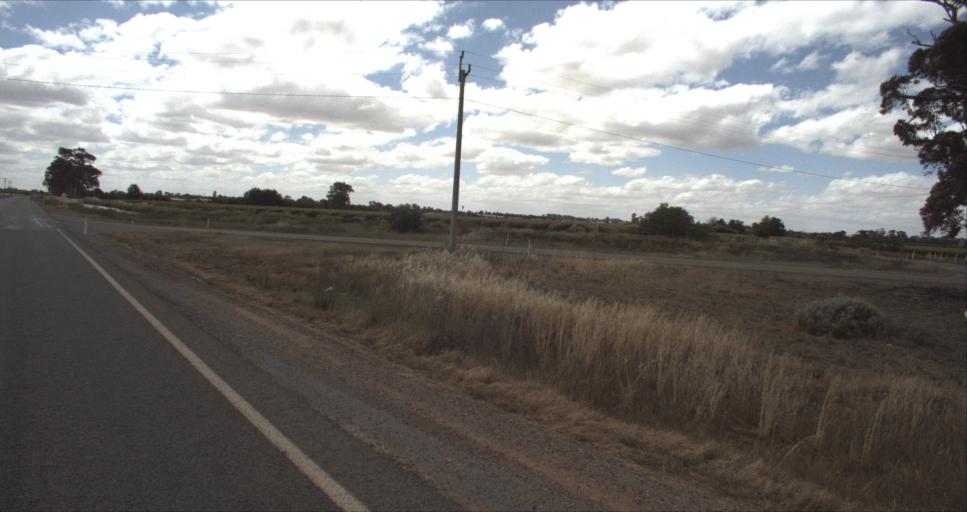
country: AU
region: New South Wales
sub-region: Leeton
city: Leeton
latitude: -34.5803
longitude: 146.3997
